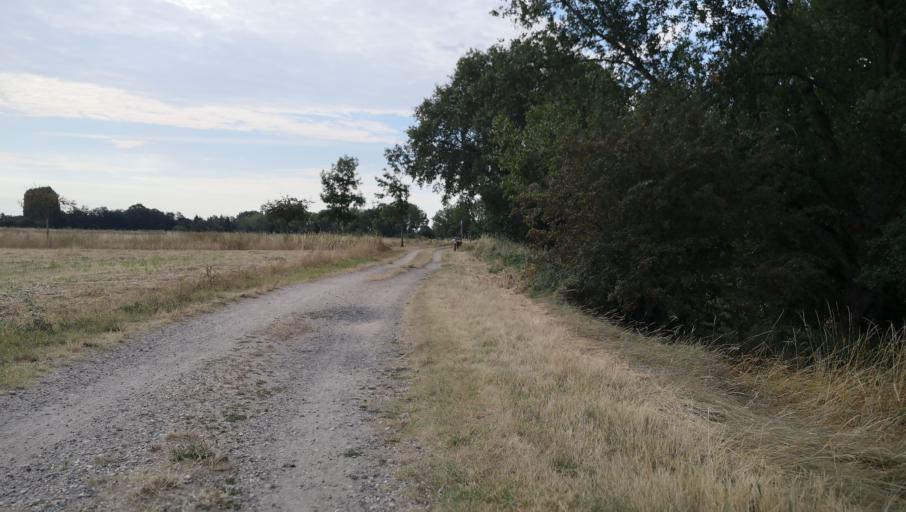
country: FR
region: Centre
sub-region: Departement du Loiret
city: Checy
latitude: 47.8886
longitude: 2.0174
